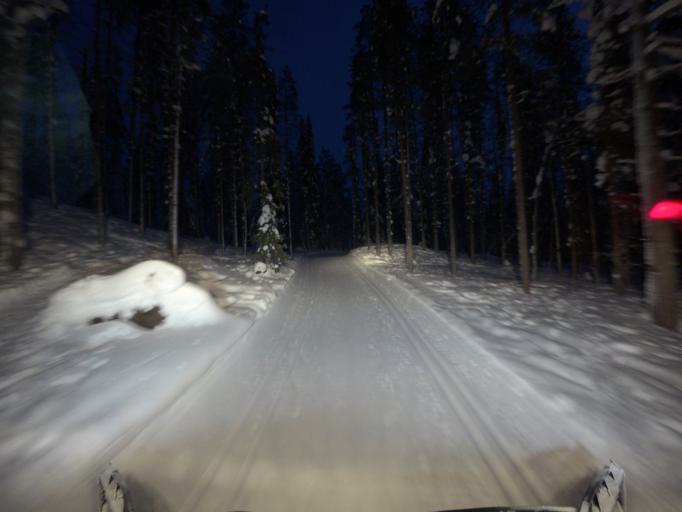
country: FI
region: Lapland
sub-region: Tunturi-Lappi
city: Kolari
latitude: 67.5996
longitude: 24.1131
